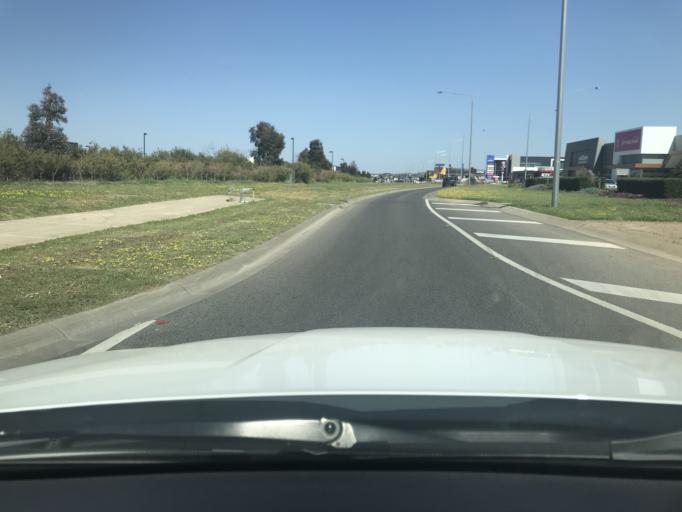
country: AU
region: Victoria
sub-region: Hume
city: Roxburgh Park
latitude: -37.5903
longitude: 144.9110
